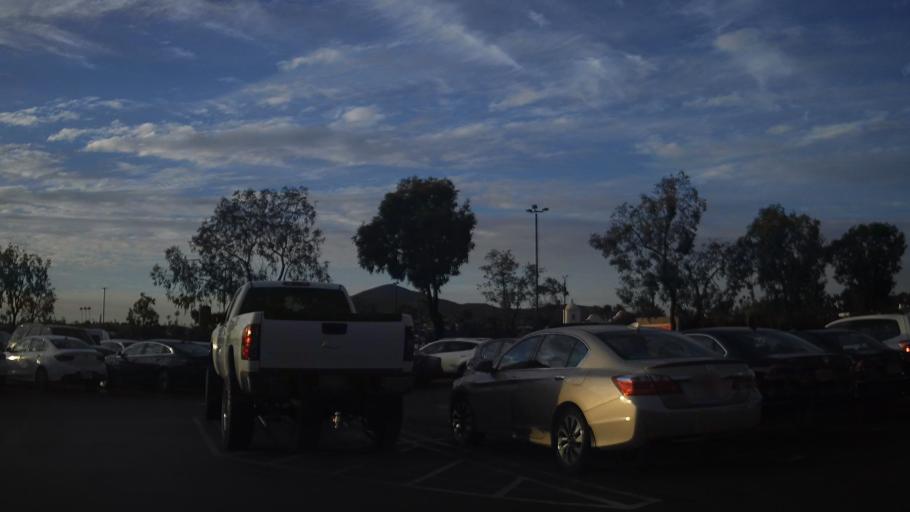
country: US
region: California
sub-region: San Diego County
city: La Mesa
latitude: 32.7792
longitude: -117.0108
